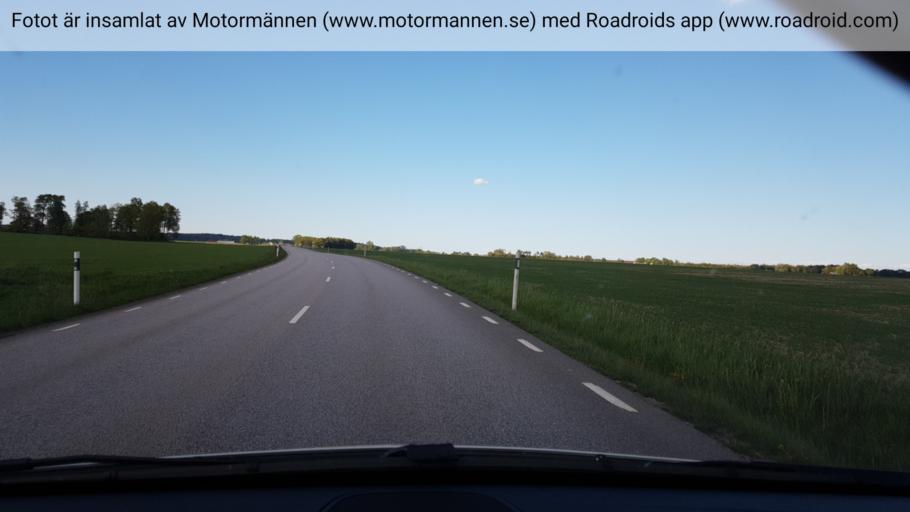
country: SE
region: Vaestra Goetaland
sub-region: Lidkopings Kommun
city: Lidkoping
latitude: 58.4601
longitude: 13.0841
